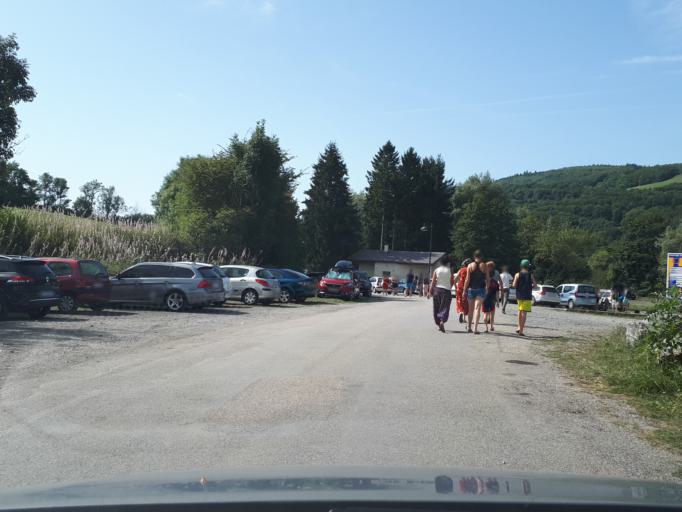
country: FR
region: Rhone-Alpes
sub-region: Departement de l'Isere
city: Pierre-Chatel
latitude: 44.9965
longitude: 5.7764
